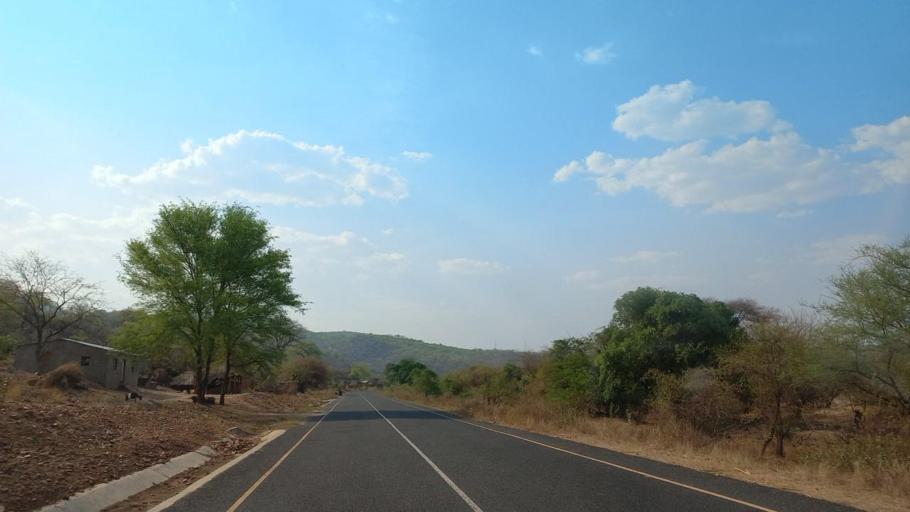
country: ZM
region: Lusaka
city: Luangwa
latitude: -15.0284
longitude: 30.2269
